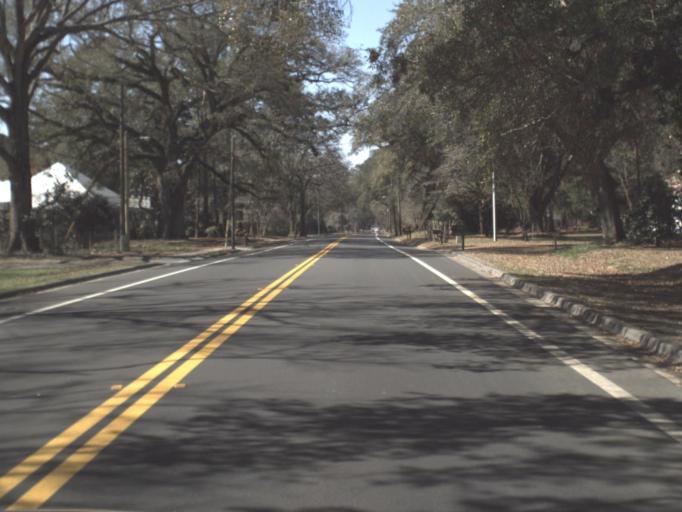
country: US
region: Florida
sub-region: Jackson County
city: Malone
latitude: 30.8699
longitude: -85.1526
